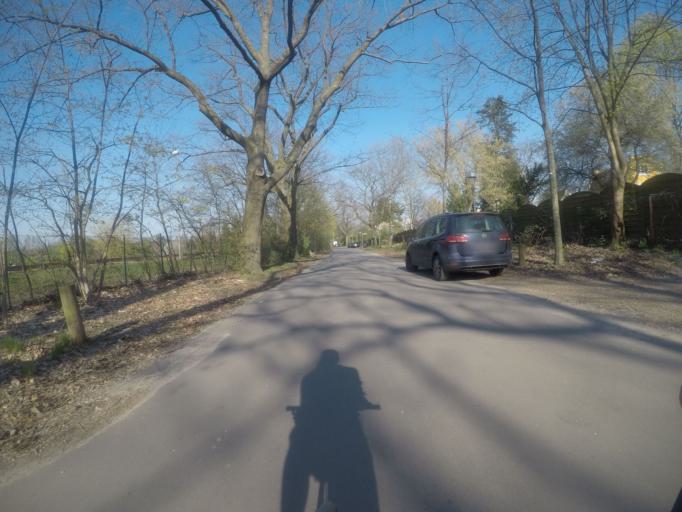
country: DE
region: Berlin
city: Zehlendorf Bezirk
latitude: 52.4294
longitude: 13.2400
